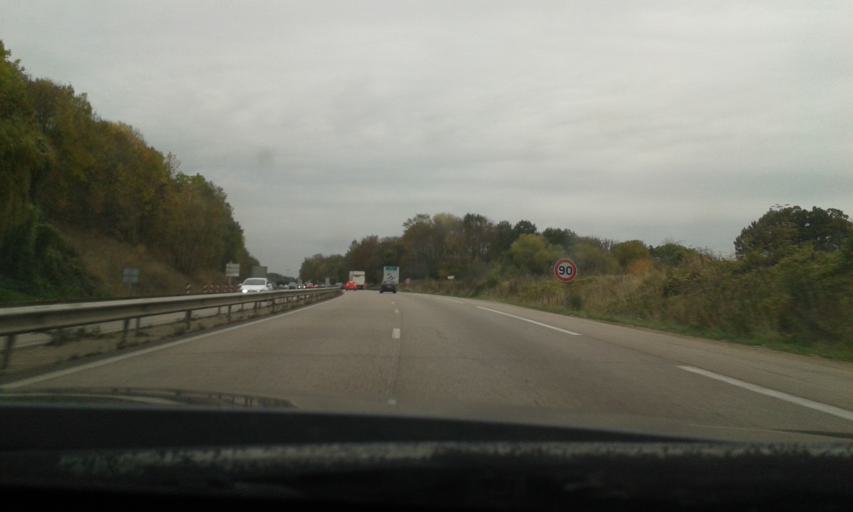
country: FR
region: Haute-Normandie
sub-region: Departement de la Seine-Maritime
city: Oissel
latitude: 49.3425
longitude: 1.0754
